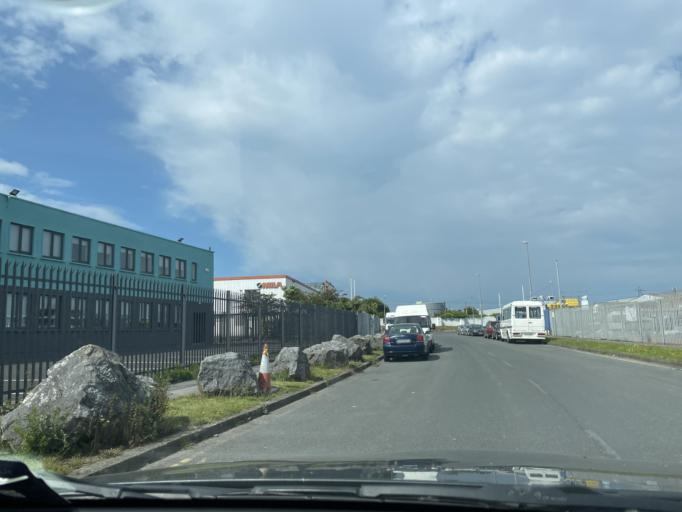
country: IE
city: Bayside
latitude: 53.3909
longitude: -6.1519
